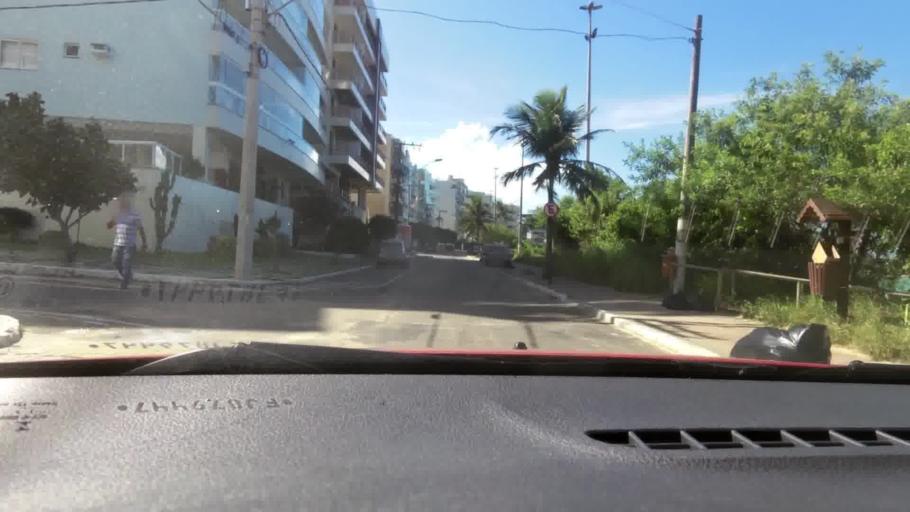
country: BR
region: Espirito Santo
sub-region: Guarapari
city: Guarapari
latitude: -20.7307
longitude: -40.5287
